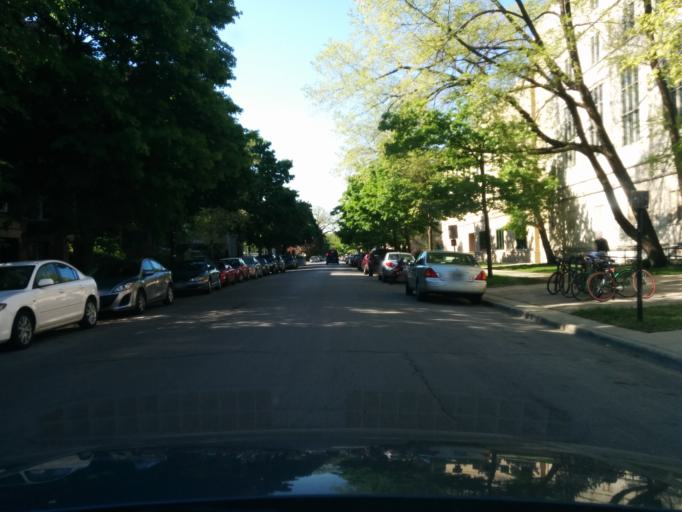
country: US
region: Illinois
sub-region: Cook County
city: Evanston
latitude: 42.0454
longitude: -87.6851
